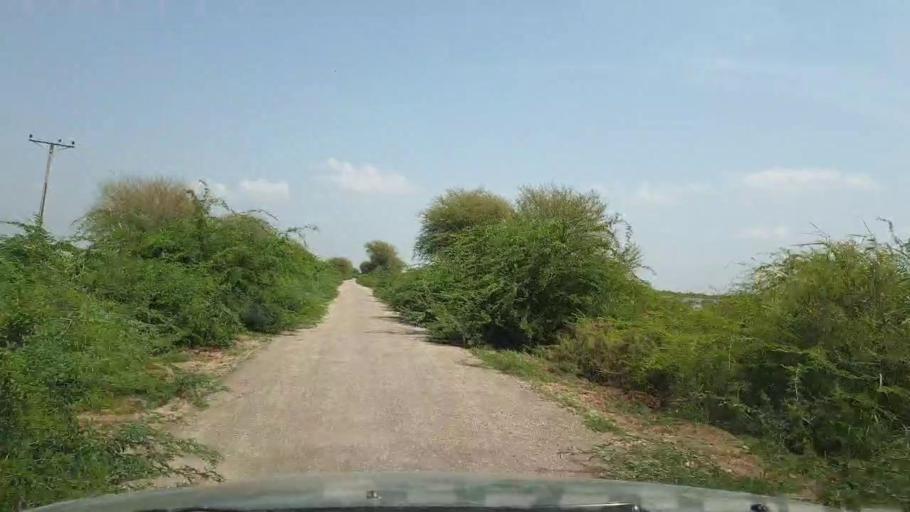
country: PK
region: Sindh
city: Rajo Khanani
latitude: 25.0275
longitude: 68.9266
